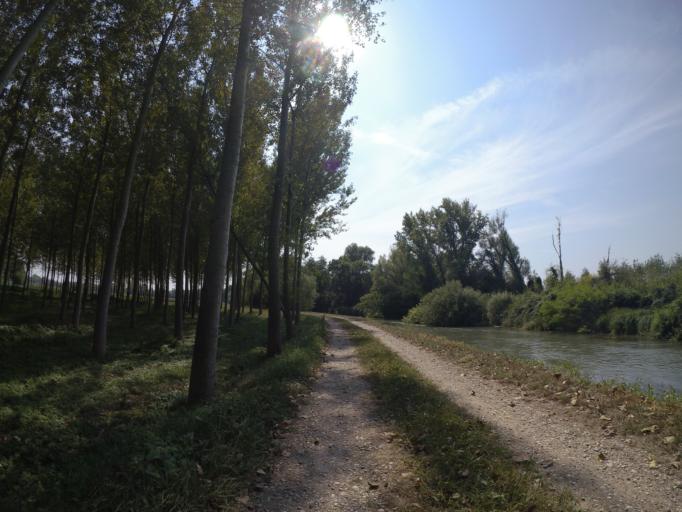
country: IT
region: Friuli Venezia Giulia
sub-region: Provincia di Udine
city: Varmo
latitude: 45.9109
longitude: 13.0190
